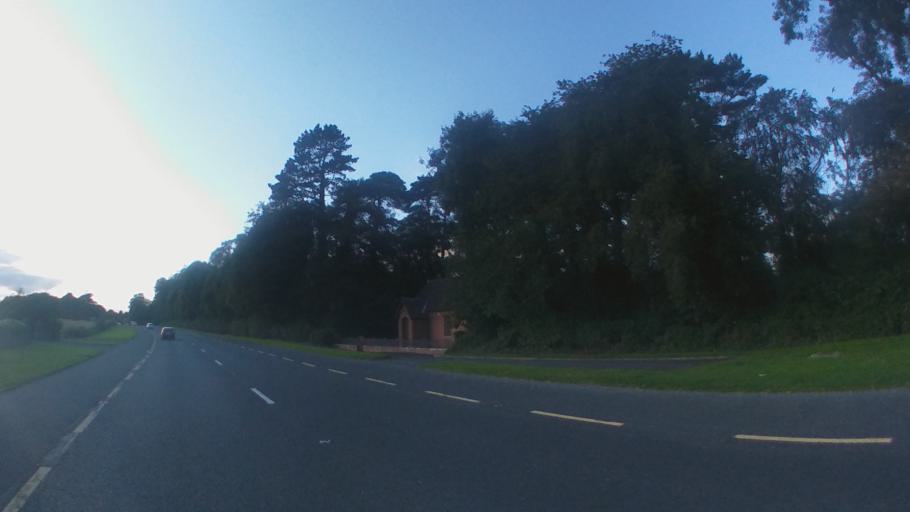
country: IE
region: Leinster
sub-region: Lu
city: Blackrock
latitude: 54.0305
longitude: -6.3548
